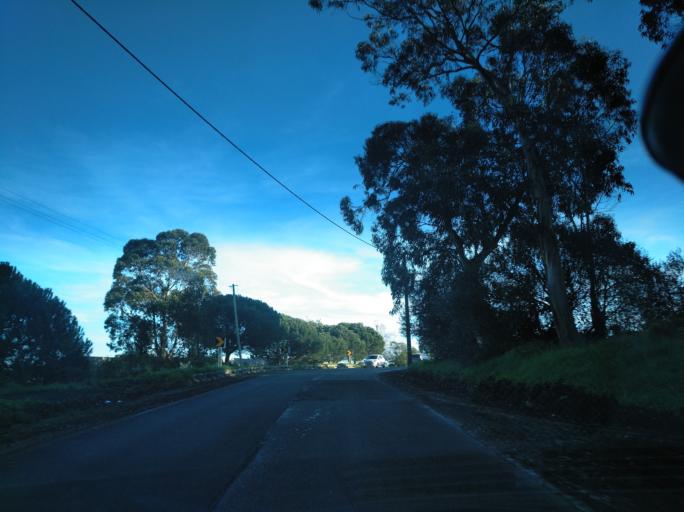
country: PT
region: Lisbon
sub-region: Sintra
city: Sintra
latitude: 38.8201
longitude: -9.3675
